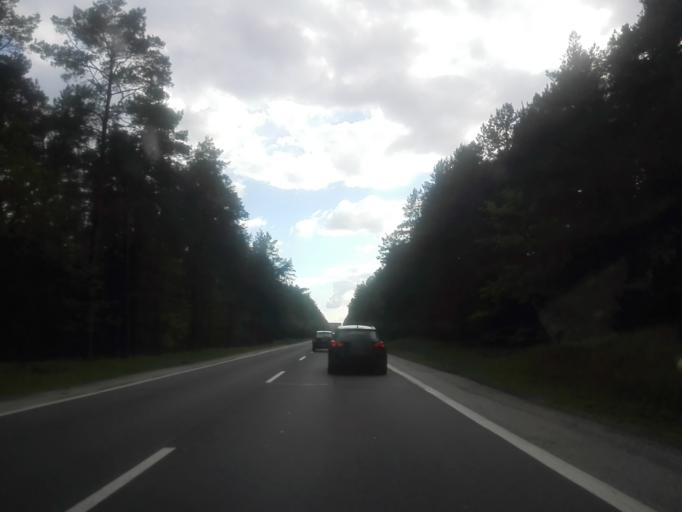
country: PL
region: Masovian Voivodeship
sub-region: Powiat ostrowski
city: Brok
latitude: 52.7342
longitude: 21.7424
